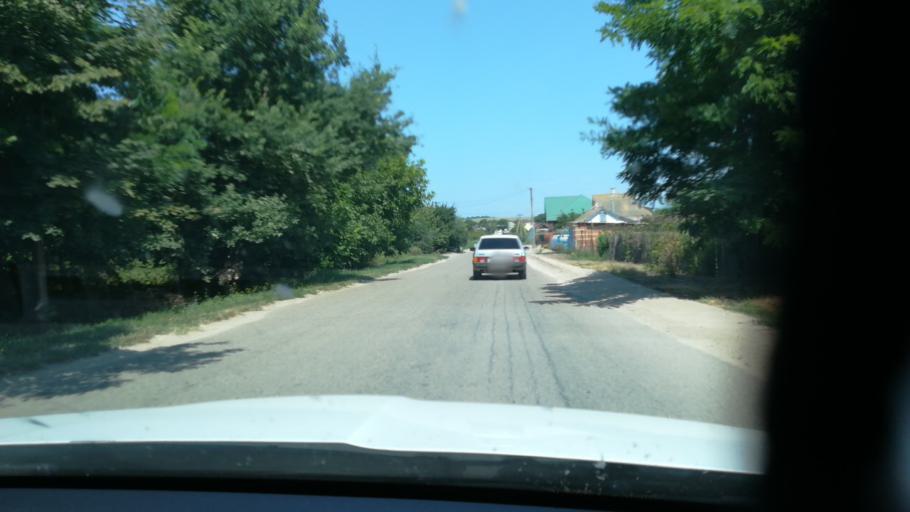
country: RU
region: Krasnodarskiy
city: Starotitarovskaya
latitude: 45.2088
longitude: 37.1457
